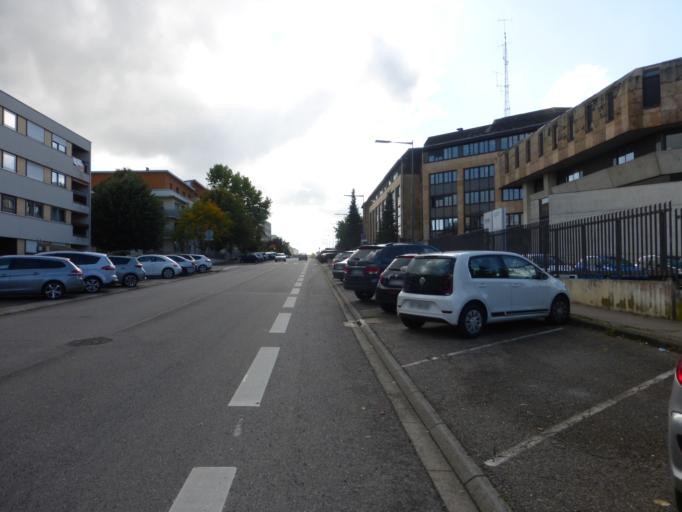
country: FR
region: Lorraine
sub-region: Departement de Meurthe-et-Moselle
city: Villers-les-Nancy
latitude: 48.6759
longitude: 6.1576
